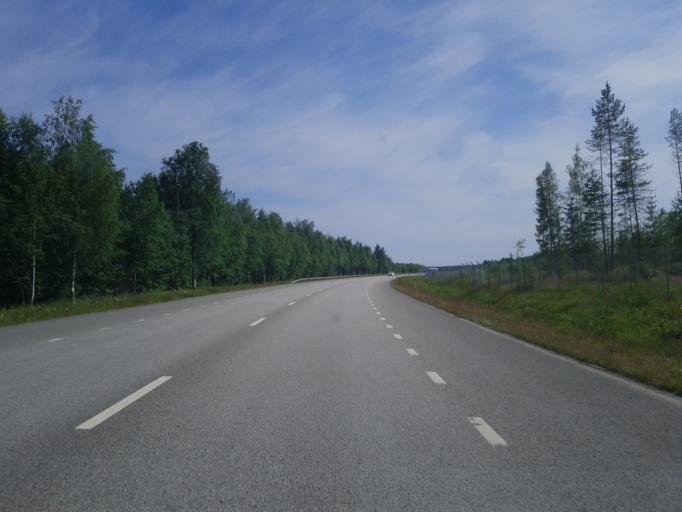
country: SE
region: Vaesterbotten
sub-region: Umea Kommun
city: Umea
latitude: 63.7863
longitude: 20.3028
